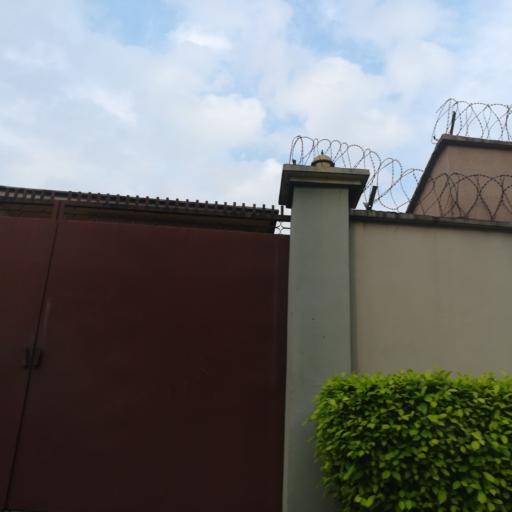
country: NG
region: Rivers
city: Port Harcourt
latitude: 4.8428
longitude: 7.0551
